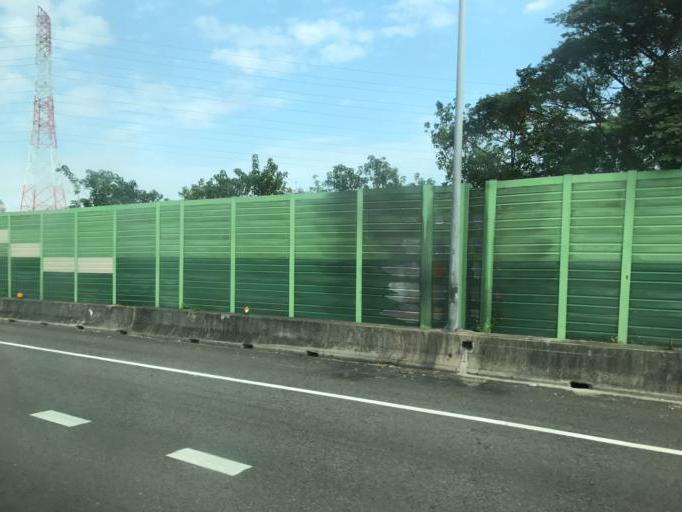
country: TW
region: Taiwan
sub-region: Hsinchu
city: Zhubei
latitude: 24.8056
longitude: 121.0100
